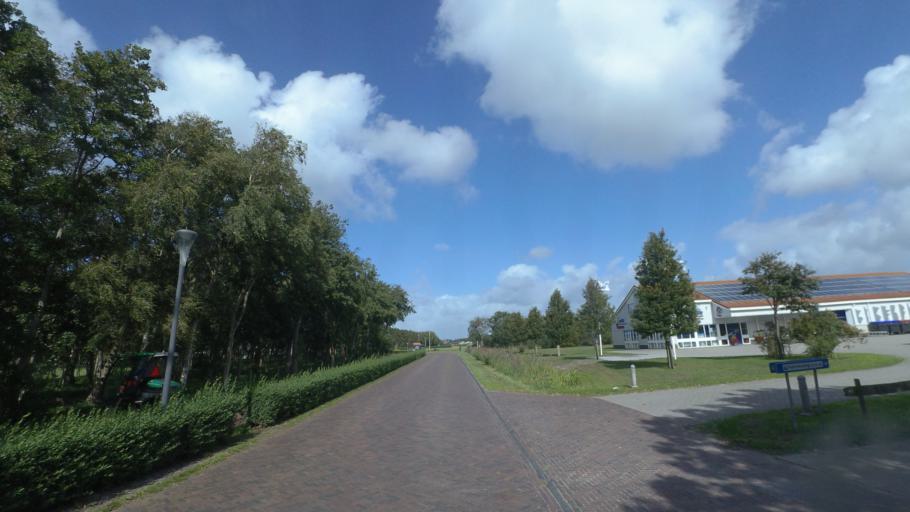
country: NL
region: Friesland
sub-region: Gemeente Ameland
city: Hollum
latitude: 53.4448
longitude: 5.6406
